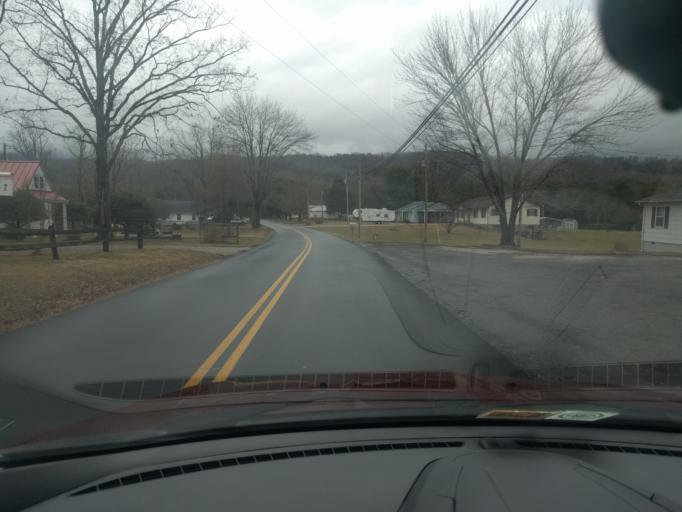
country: US
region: Virginia
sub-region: Botetourt County
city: Fincastle
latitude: 37.5457
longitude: -79.8751
